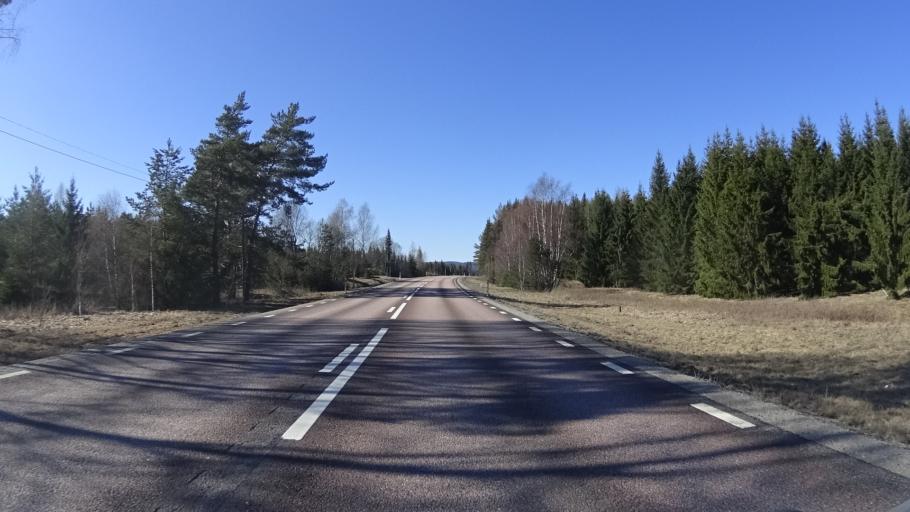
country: SE
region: Vaermland
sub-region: Sunne Kommun
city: Sunne
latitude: 59.6267
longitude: 12.9566
